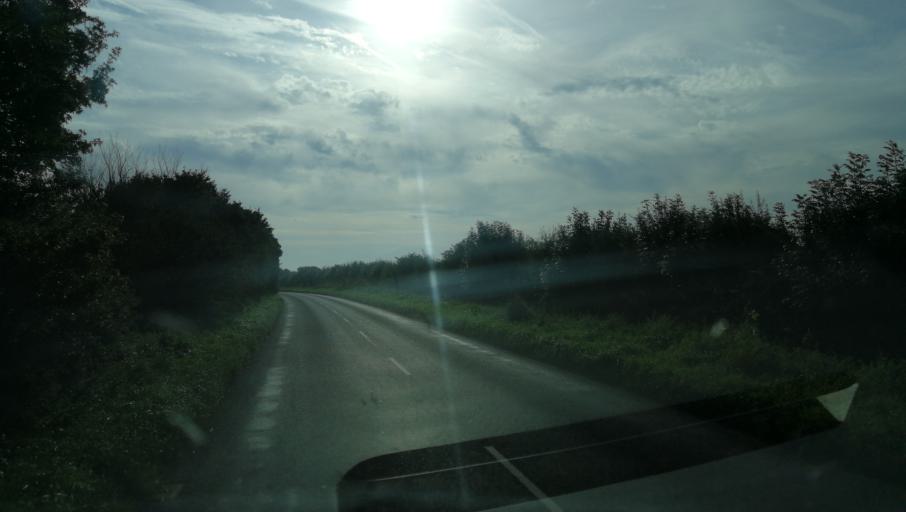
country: GB
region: England
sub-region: Oxfordshire
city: Adderbury
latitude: 52.0110
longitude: -1.3379
